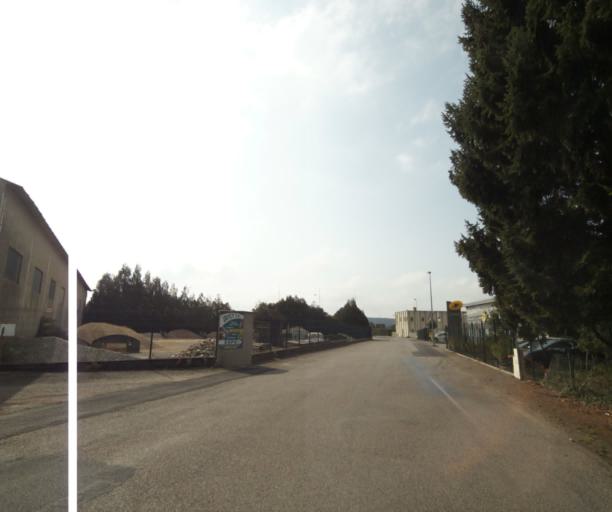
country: FR
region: Bourgogne
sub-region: Departement de Saone-et-Loire
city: Charolles
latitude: 46.4323
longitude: 4.2695
